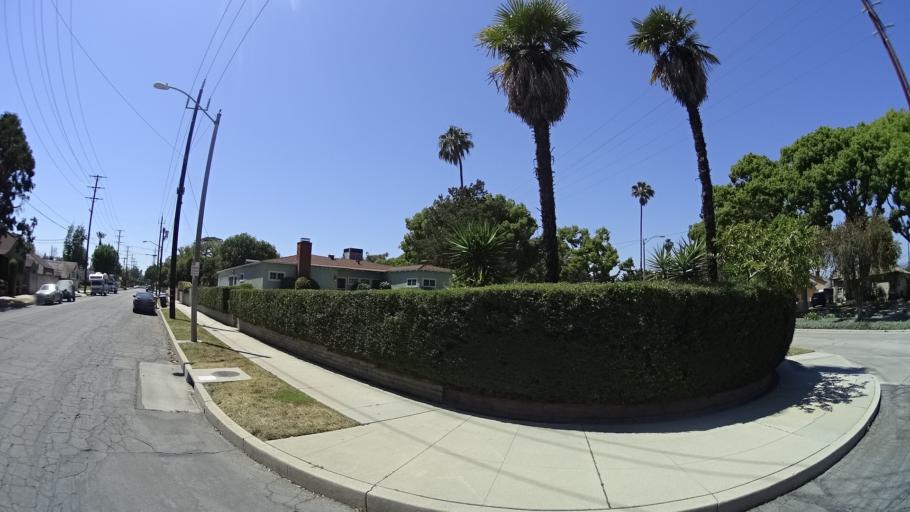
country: US
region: California
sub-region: Los Angeles County
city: North Hollywood
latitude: 34.1776
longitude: -118.3546
